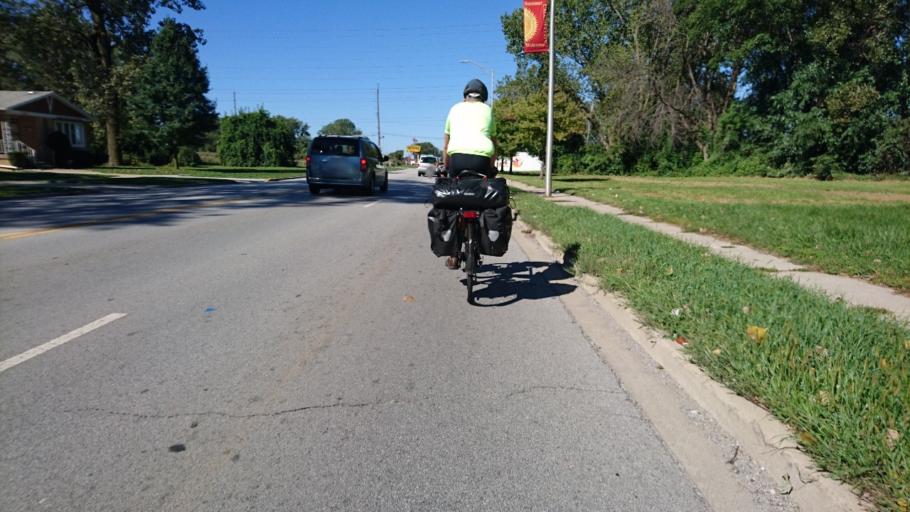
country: US
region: Illinois
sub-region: Cook County
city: Burnham
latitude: 41.6228
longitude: -87.5469
